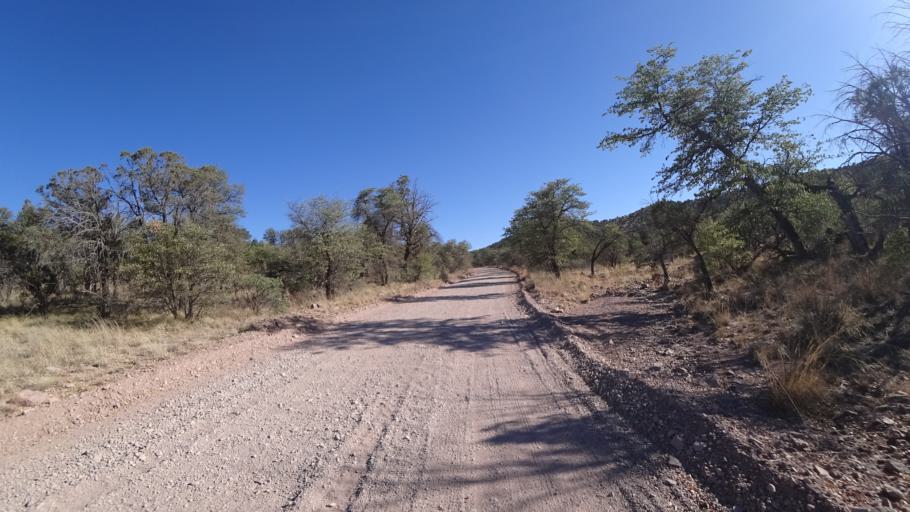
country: US
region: Arizona
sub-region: Cochise County
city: Huachuca City
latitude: 31.5077
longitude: -110.5579
